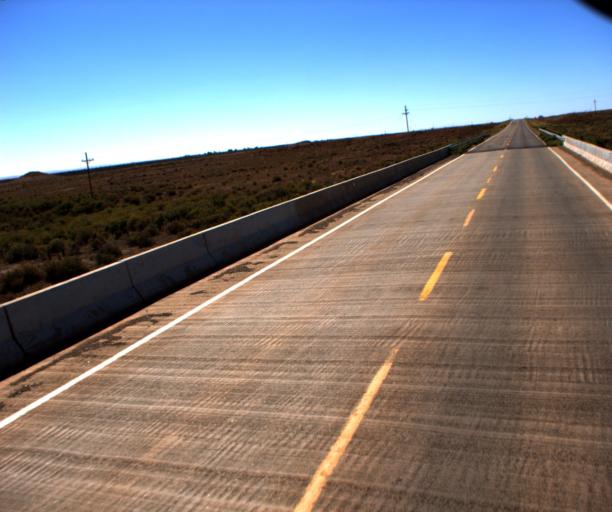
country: US
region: Arizona
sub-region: Coconino County
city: LeChee
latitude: 35.2952
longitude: -110.9915
